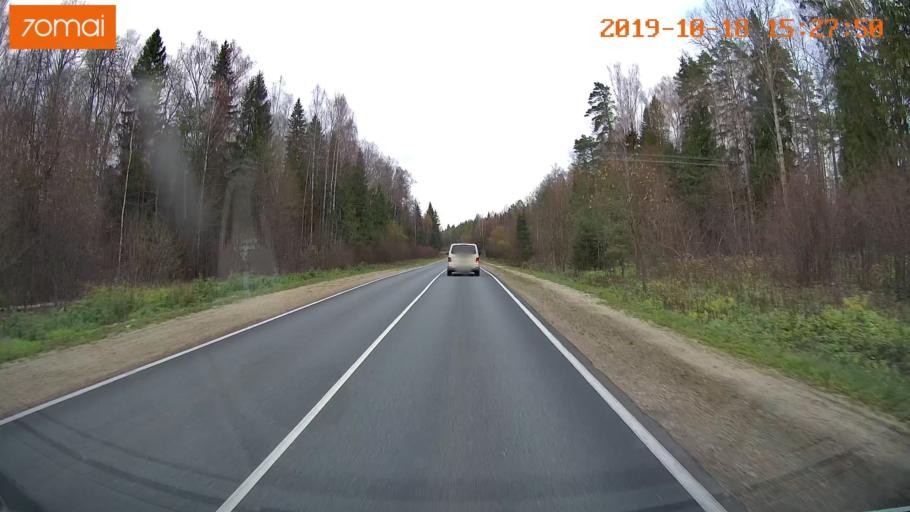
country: RU
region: Vladimir
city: Anopino
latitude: 55.7587
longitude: 40.6725
